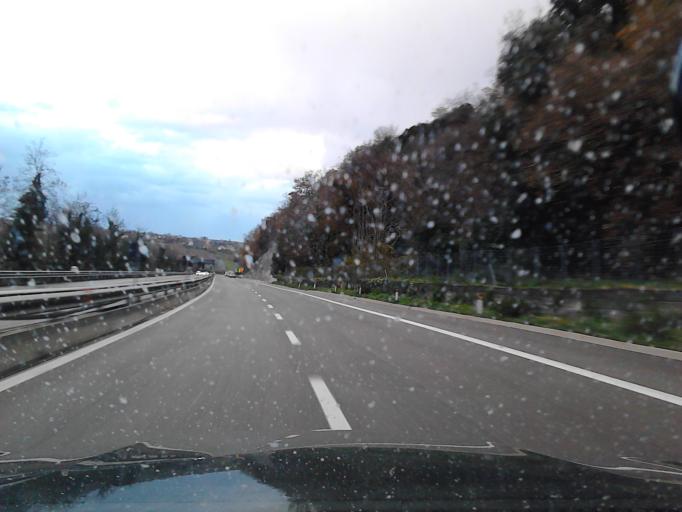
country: IT
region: Abruzzo
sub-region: Provincia di Chieti
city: San Vito Chietino
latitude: 42.2753
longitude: 14.4357
